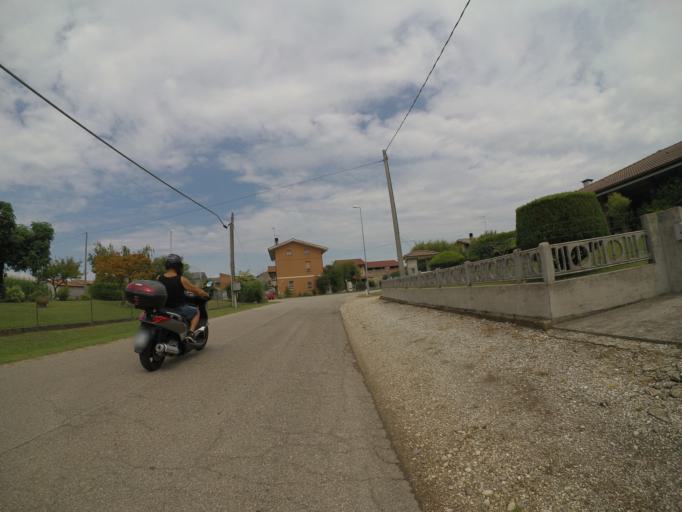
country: IT
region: Friuli Venezia Giulia
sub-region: Provincia di Udine
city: Basiliano
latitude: 45.9813
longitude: 13.0947
